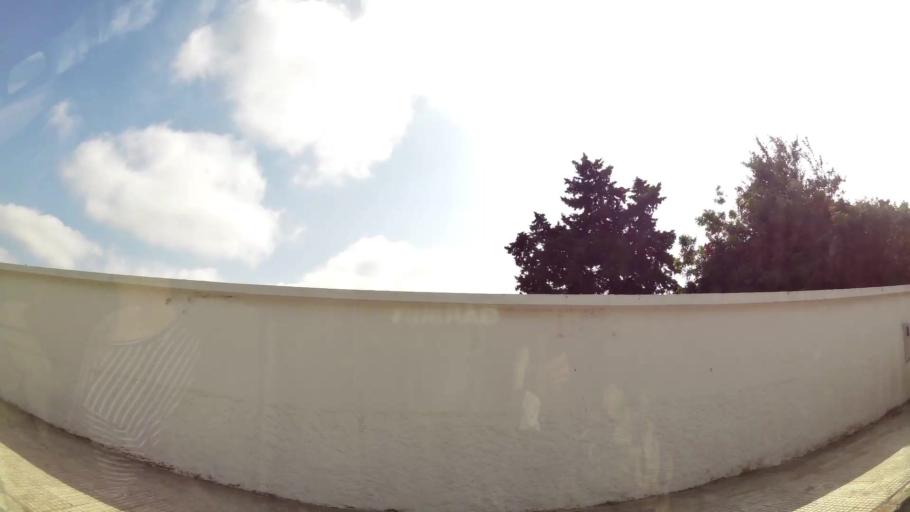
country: MA
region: Rabat-Sale-Zemmour-Zaer
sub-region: Rabat
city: Rabat
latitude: 33.9724
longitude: -6.8599
